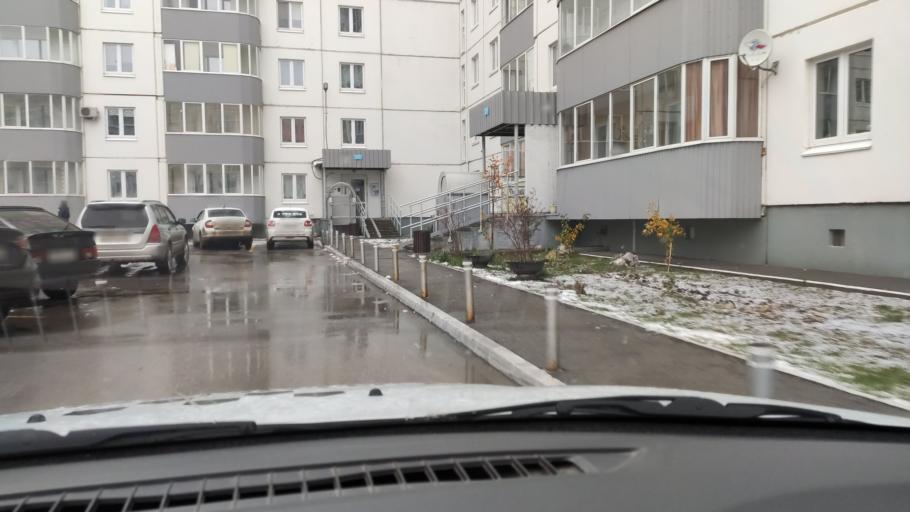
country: RU
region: Perm
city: Kondratovo
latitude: 57.9891
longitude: 56.1182
